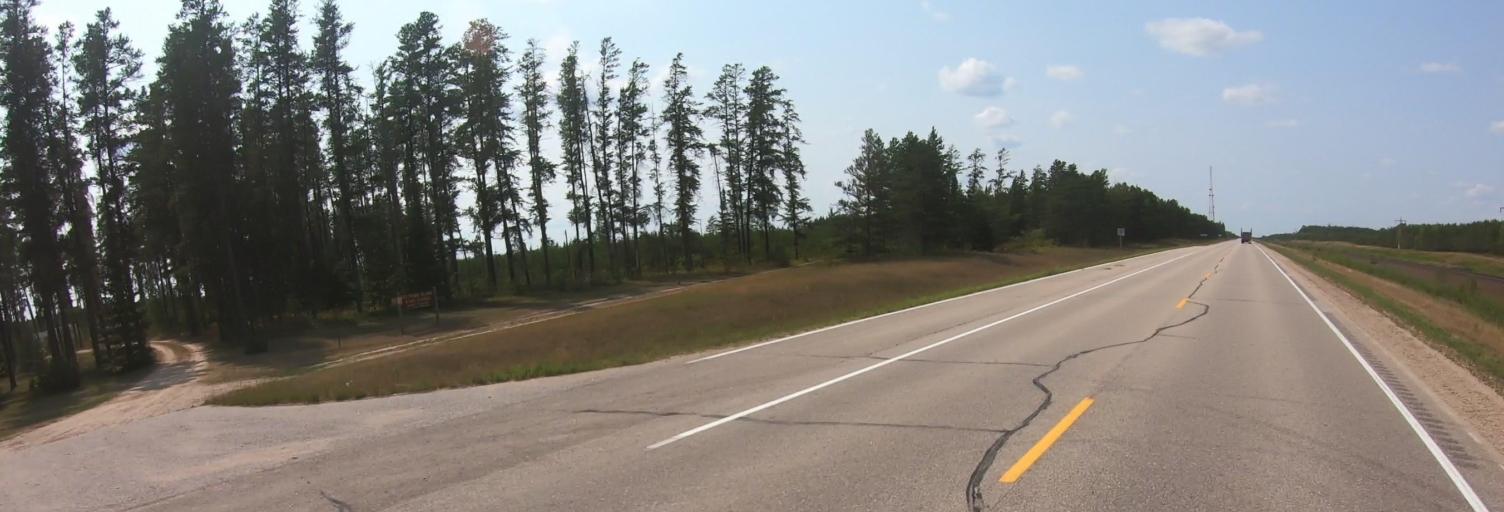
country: US
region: Minnesota
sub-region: Roseau County
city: Warroad
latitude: 48.7862
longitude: -95.0360
